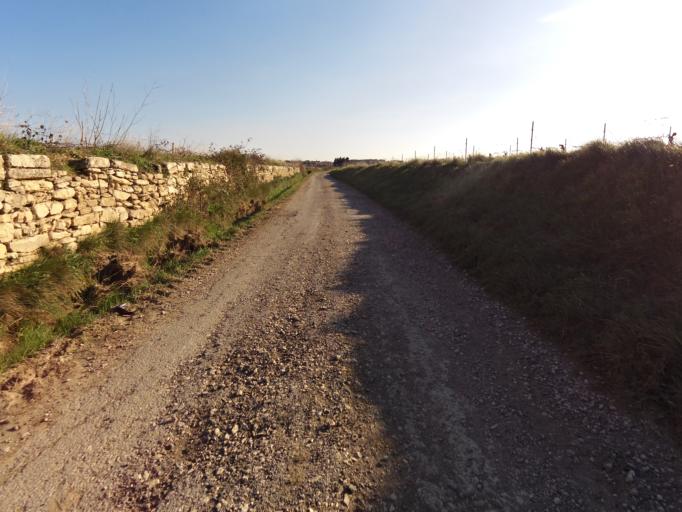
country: FR
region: Languedoc-Roussillon
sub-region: Departement du Gard
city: Aigues-Vives
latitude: 43.7518
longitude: 4.1804
